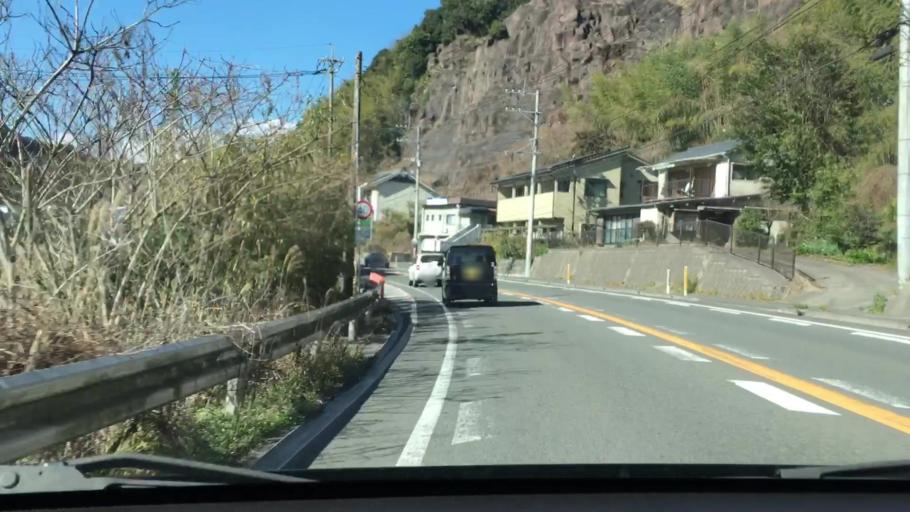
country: JP
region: Kagoshima
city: Kagoshima-shi
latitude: 31.6340
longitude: 130.5232
